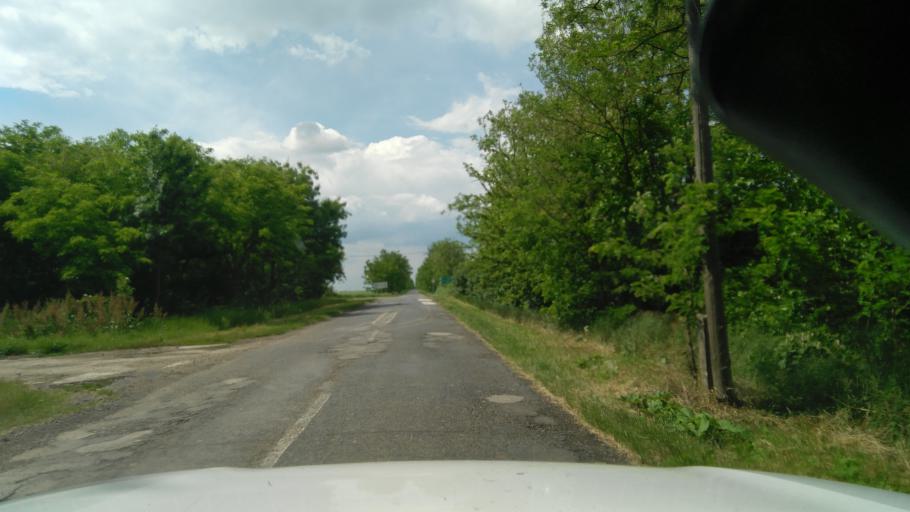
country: HU
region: Bekes
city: Magyarbanhegyes
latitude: 46.4694
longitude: 20.9441
